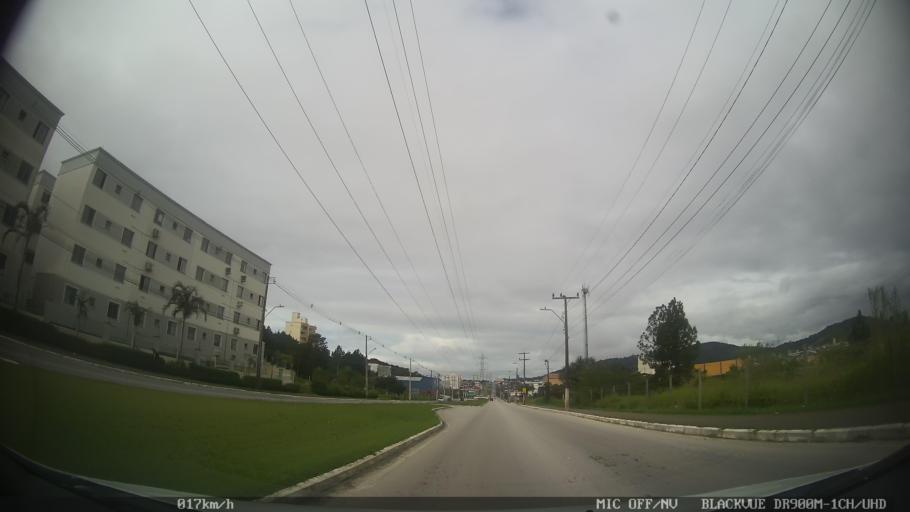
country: BR
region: Santa Catarina
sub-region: Sao Jose
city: Campinas
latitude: -27.5574
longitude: -48.6408
